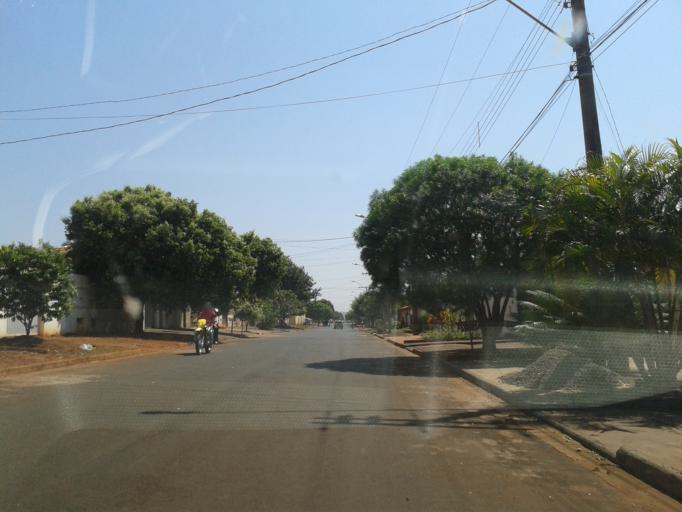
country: BR
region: Minas Gerais
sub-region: Ituiutaba
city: Ituiutaba
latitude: -18.9919
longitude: -49.4452
